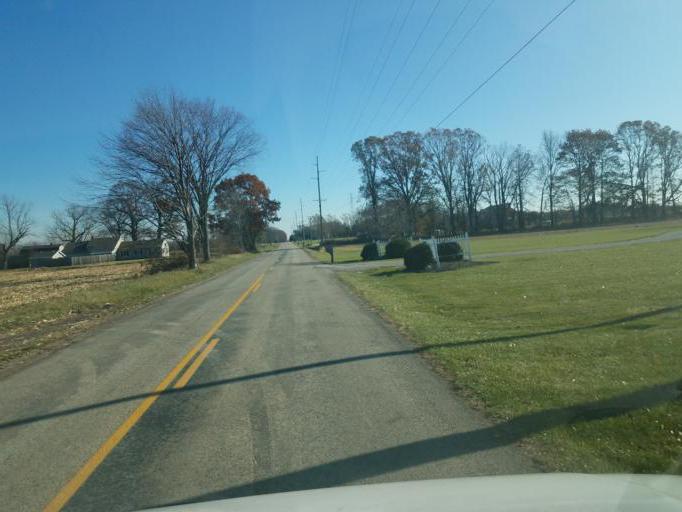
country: US
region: Ohio
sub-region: Ashland County
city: Ashland
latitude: 40.8290
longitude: -82.3410
